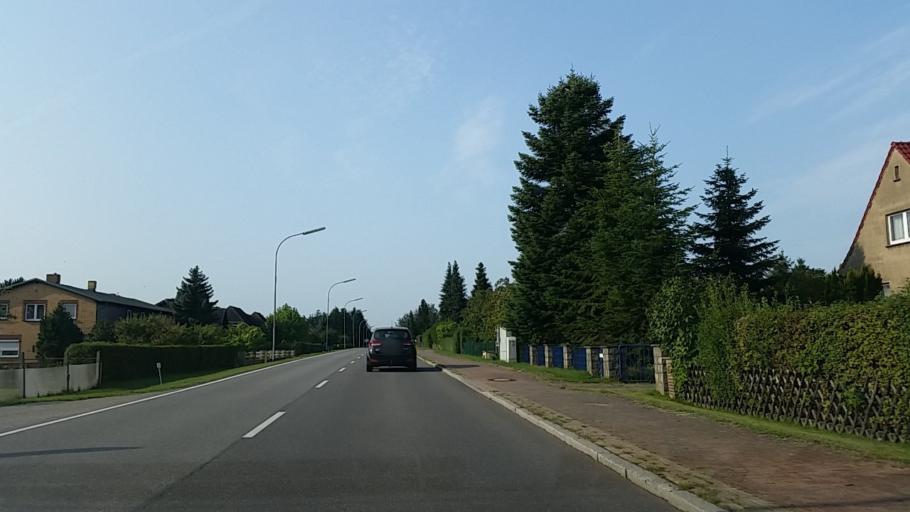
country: DE
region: Mecklenburg-Vorpommern
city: Hagenow
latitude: 53.4246
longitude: 11.1459
